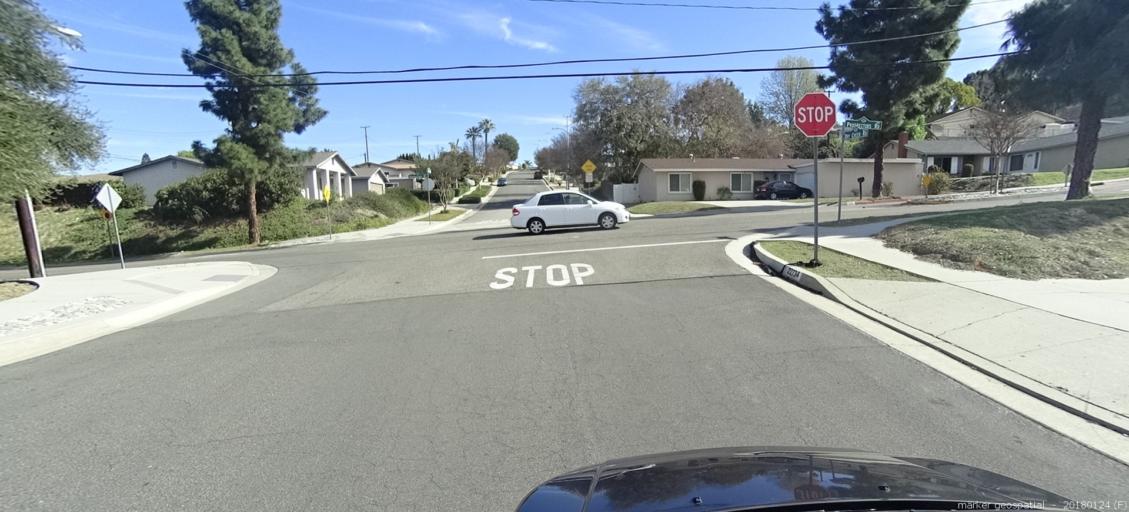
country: US
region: California
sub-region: Los Angeles County
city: Diamond Bar
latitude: 34.0294
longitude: -117.8173
